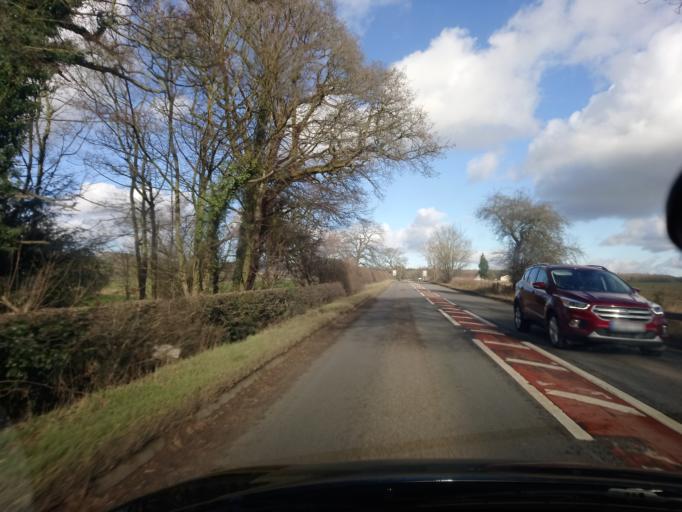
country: GB
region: England
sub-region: Shropshire
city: Clive
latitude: 52.7895
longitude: -2.7038
